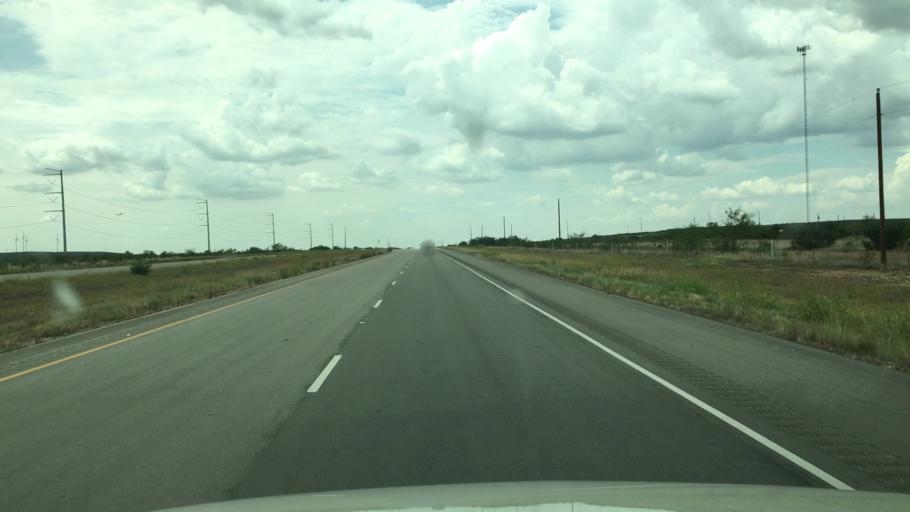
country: US
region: Texas
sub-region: Glasscock County
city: Garden City
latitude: 31.9780
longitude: -101.2513
